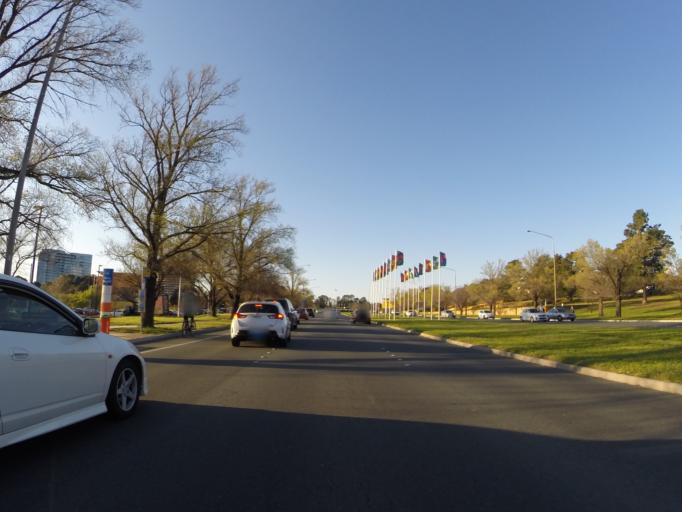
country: AU
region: Australian Capital Territory
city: Canberra
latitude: -35.2890
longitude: 149.1274
